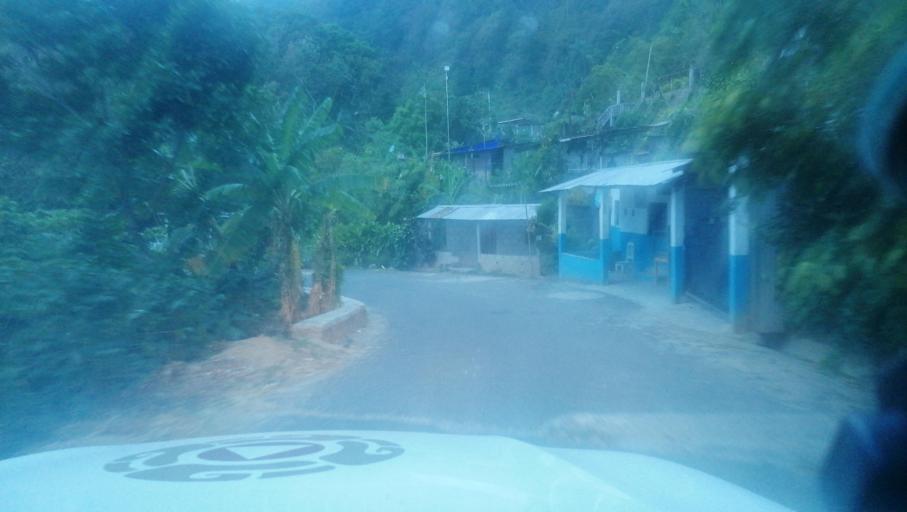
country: MX
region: Chiapas
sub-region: Cacahoatan
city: Benito Juarez
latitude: 15.1207
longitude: -92.2094
